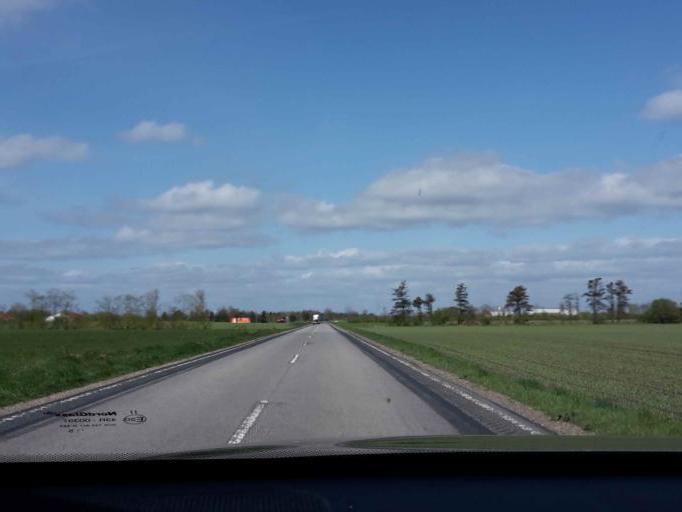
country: DK
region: South Denmark
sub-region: Billund Kommune
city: Grindsted
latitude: 55.6787
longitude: 8.9200
